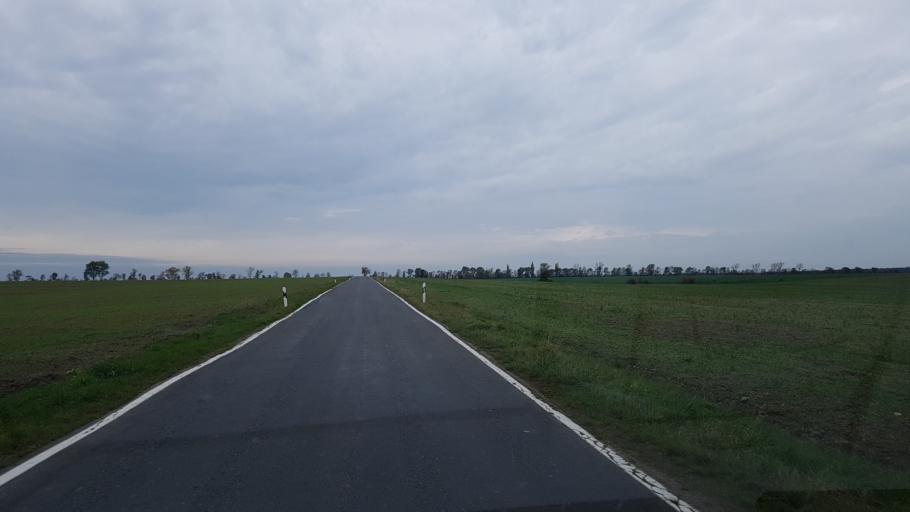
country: DE
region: Saxony
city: Dahlen
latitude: 51.3706
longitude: 12.9804
